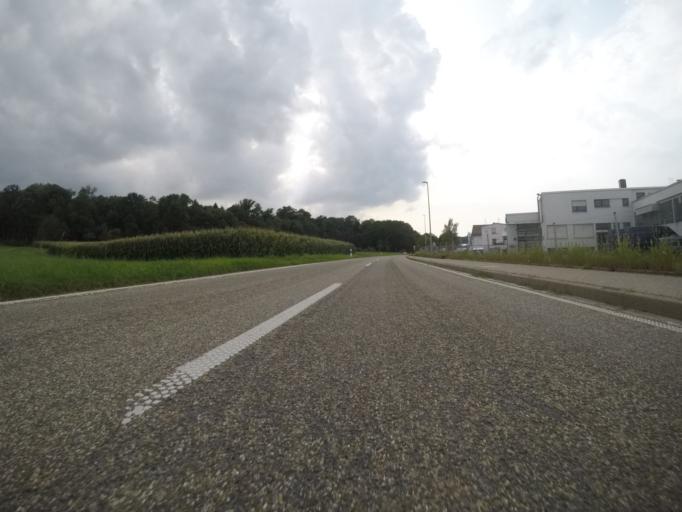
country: DE
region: Baden-Wuerttemberg
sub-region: Regierungsbezirk Stuttgart
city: Eberdingen
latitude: 48.8851
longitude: 8.9947
